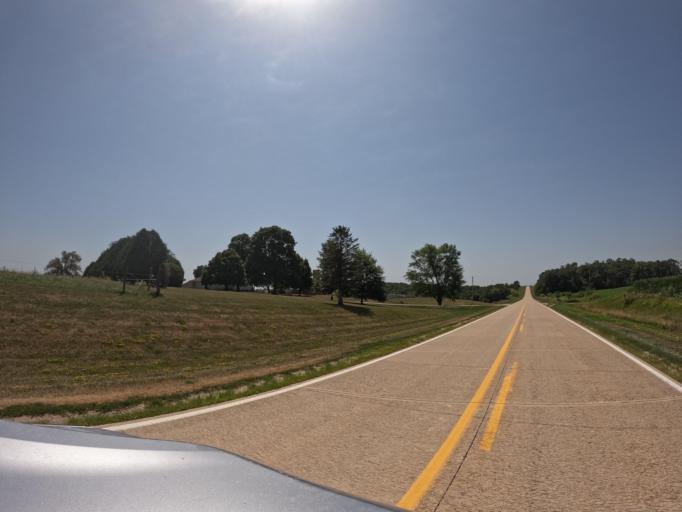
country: US
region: Iowa
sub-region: Henry County
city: Mount Pleasant
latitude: 40.8779
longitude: -91.5603
